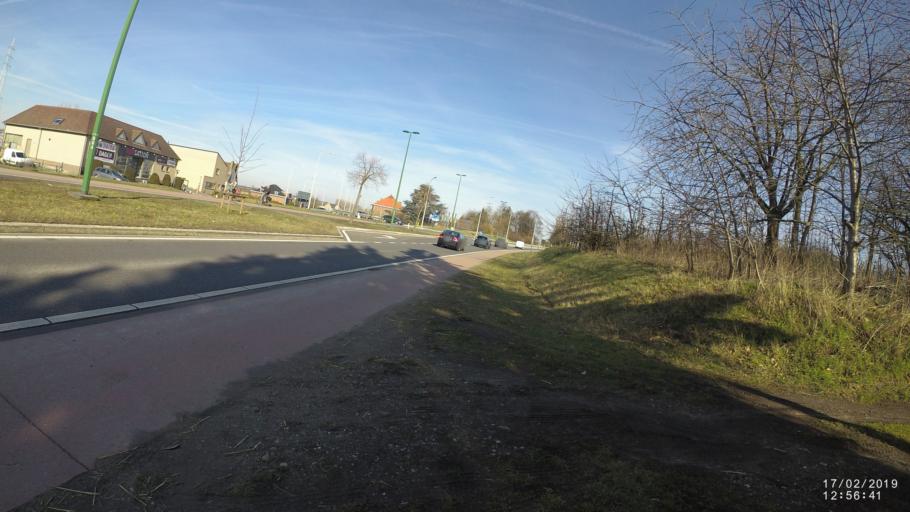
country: BE
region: Flanders
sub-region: Provincie Limburg
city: Sint-Truiden
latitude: 50.8036
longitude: 5.1809
